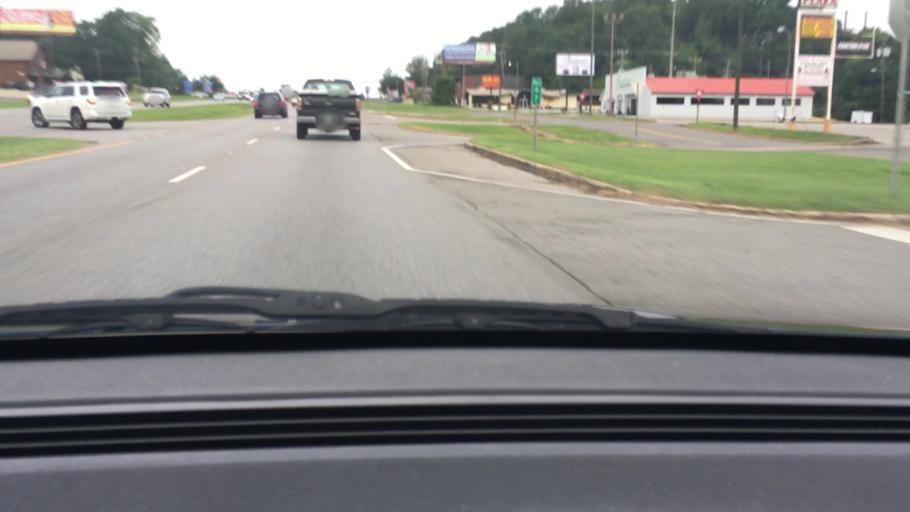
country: US
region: Alabama
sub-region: Tuscaloosa County
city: Northport
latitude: 33.2374
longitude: -87.5664
